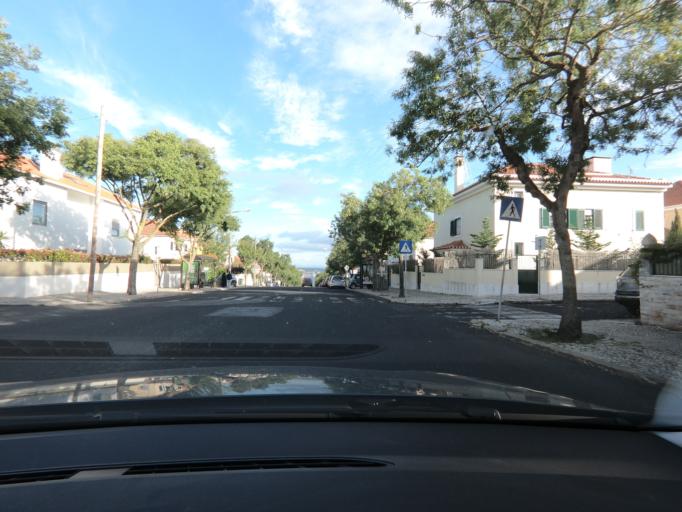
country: PT
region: Lisbon
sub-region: Oeiras
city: Alges
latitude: 38.7119
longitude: -9.2013
